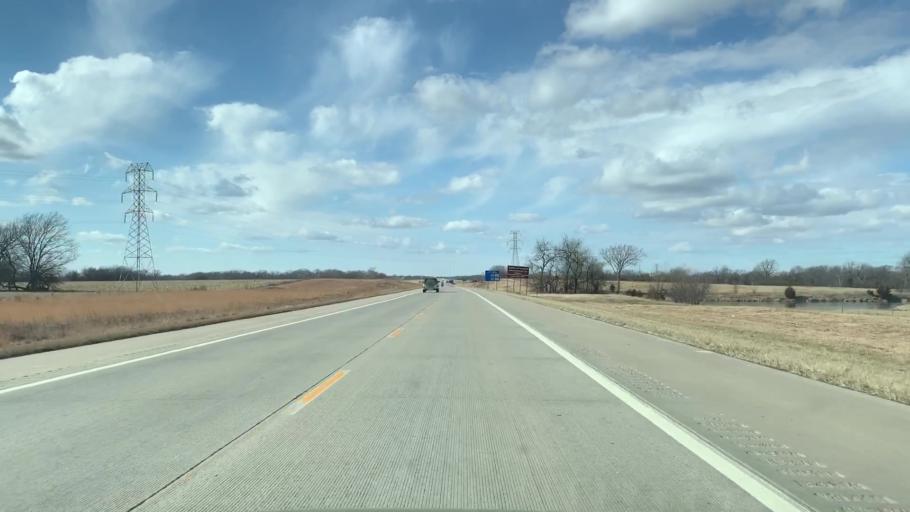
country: US
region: Kansas
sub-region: Labette County
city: Parsons
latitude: 37.3636
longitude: -95.2385
